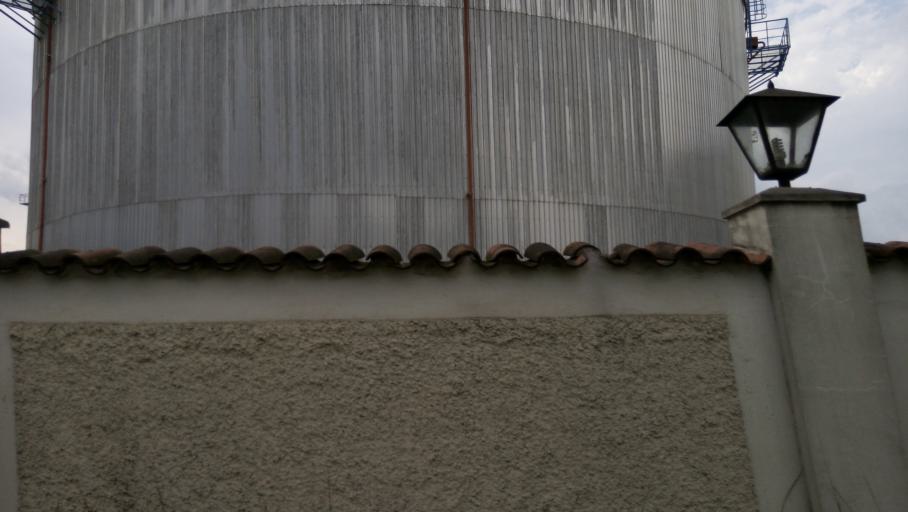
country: GE
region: Ajaria
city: Batumi
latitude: 41.6439
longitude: 41.6669
